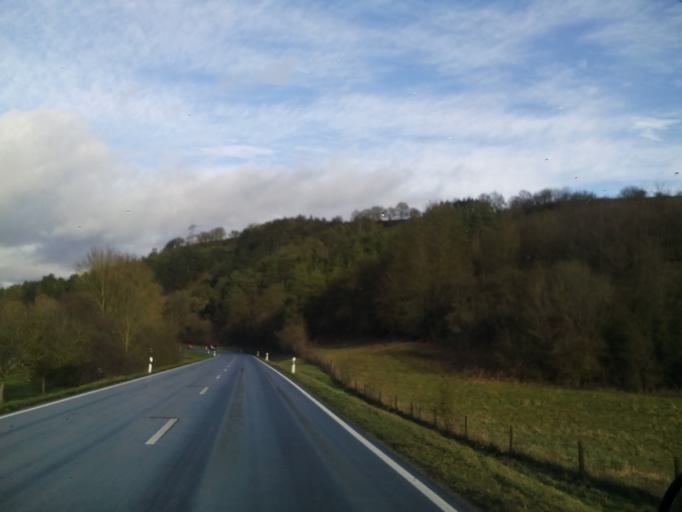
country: DE
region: Bavaria
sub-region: Regierungsbezirk Unterfranken
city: Eussenheim
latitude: 49.9931
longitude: 9.8130
